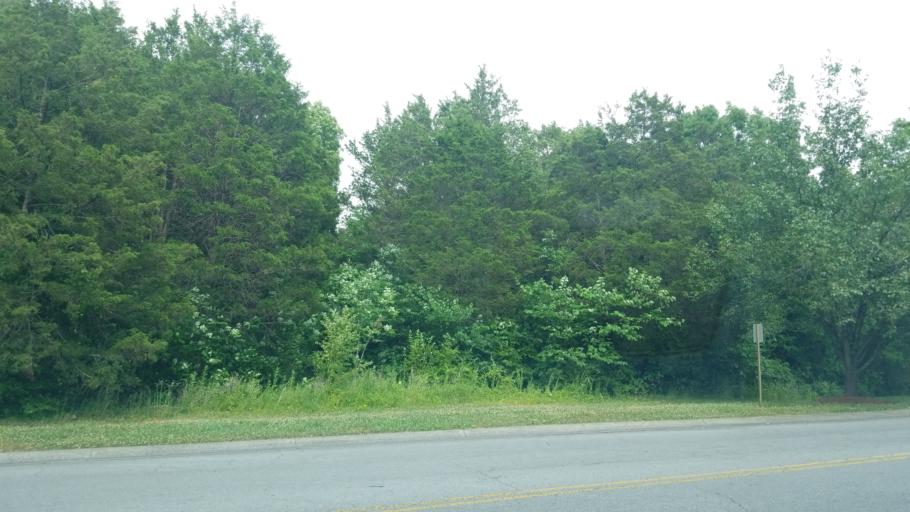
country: US
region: Tennessee
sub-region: Rutherford County
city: La Vergne
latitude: 36.0690
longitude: -86.5855
